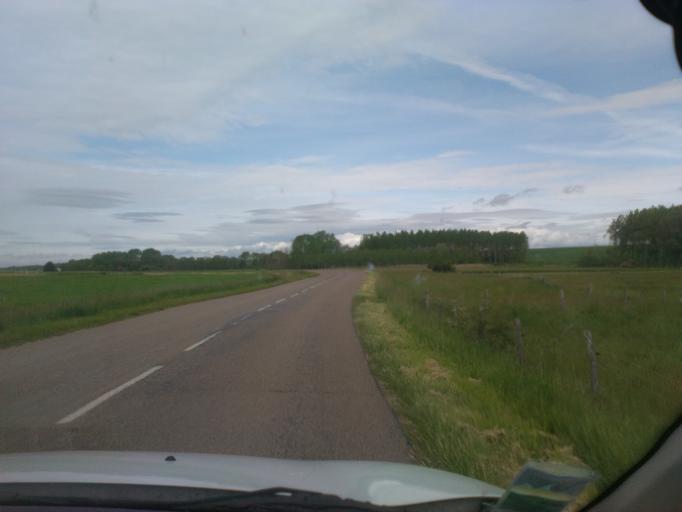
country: FR
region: Champagne-Ardenne
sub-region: Departement de l'Aube
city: Marigny-le-Chatel
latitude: 48.3562
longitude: 3.6833
